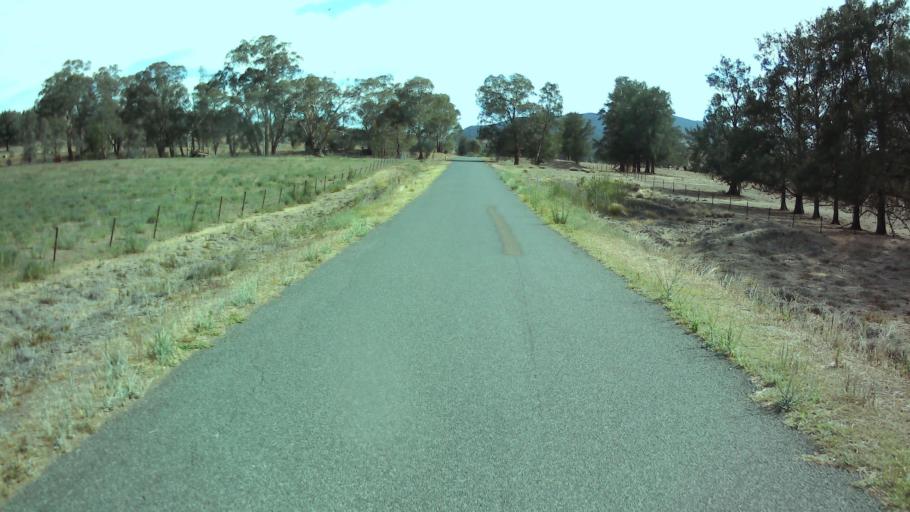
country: AU
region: New South Wales
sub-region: Weddin
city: Grenfell
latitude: -33.8128
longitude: 148.2923
